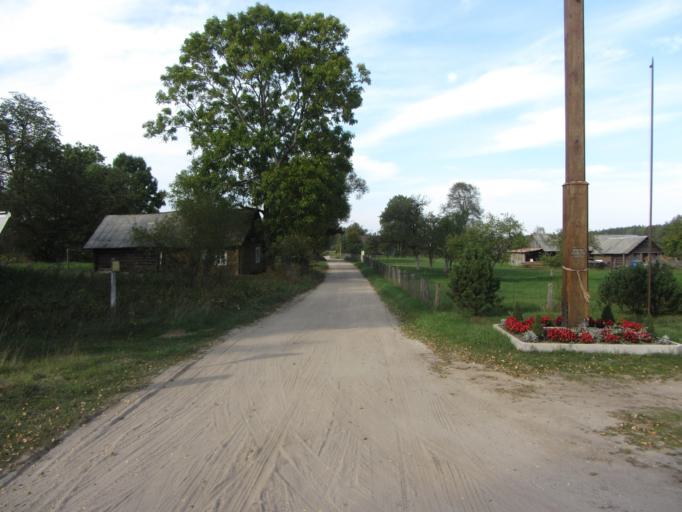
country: LT
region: Alytaus apskritis
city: Varena
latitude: 54.0228
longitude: 24.3313
